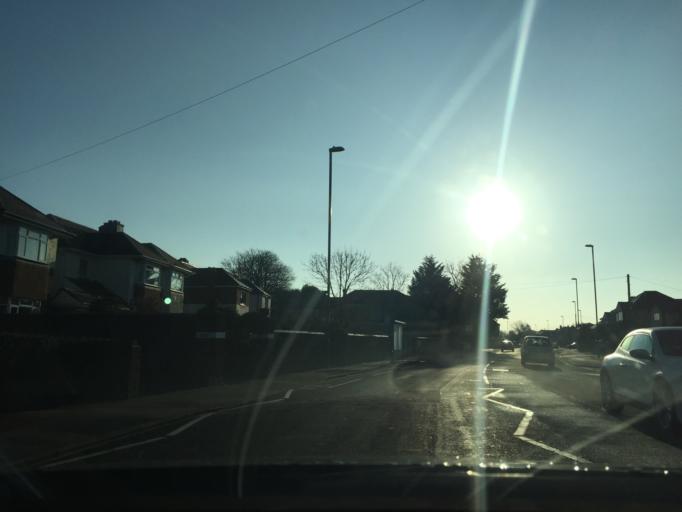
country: GB
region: England
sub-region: Hampshire
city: Gosport
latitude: 50.7941
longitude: -1.1588
